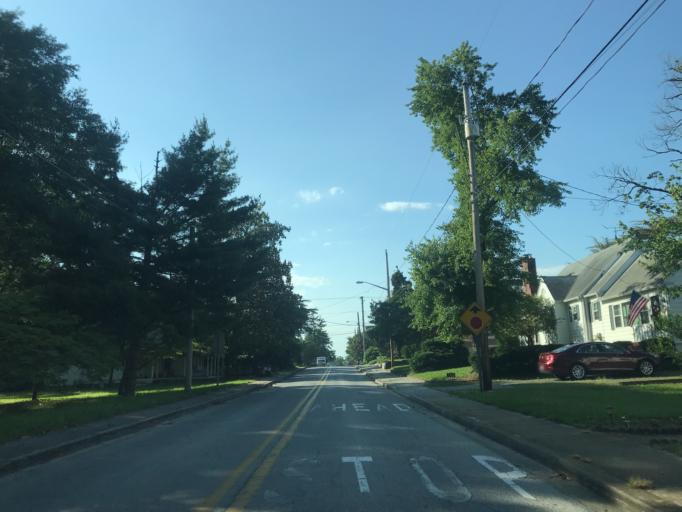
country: US
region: Maryland
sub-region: Wicomico County
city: Hebron
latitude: 38.5373
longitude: -75.7177
